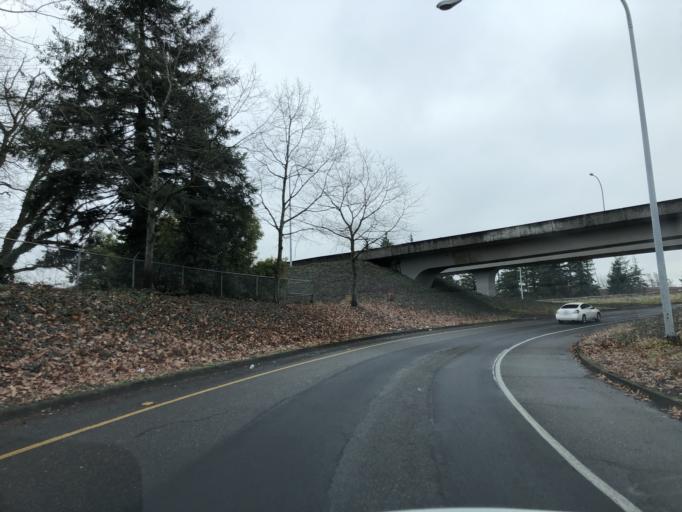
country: US
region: Washington
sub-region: Clark County
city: Vancouver
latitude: 45.6232
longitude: -122.6688
